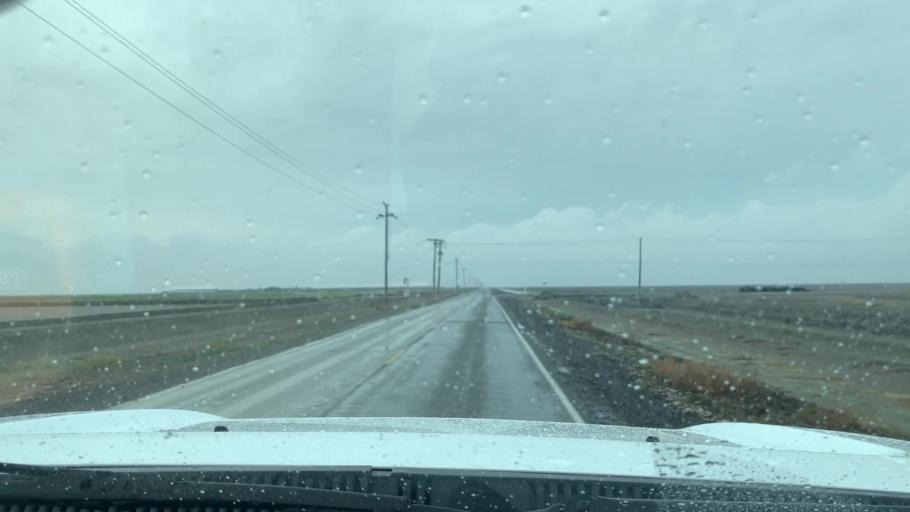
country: US
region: California
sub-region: Tulare County
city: Alpaugh
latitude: 35.9503
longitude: -119.5731
